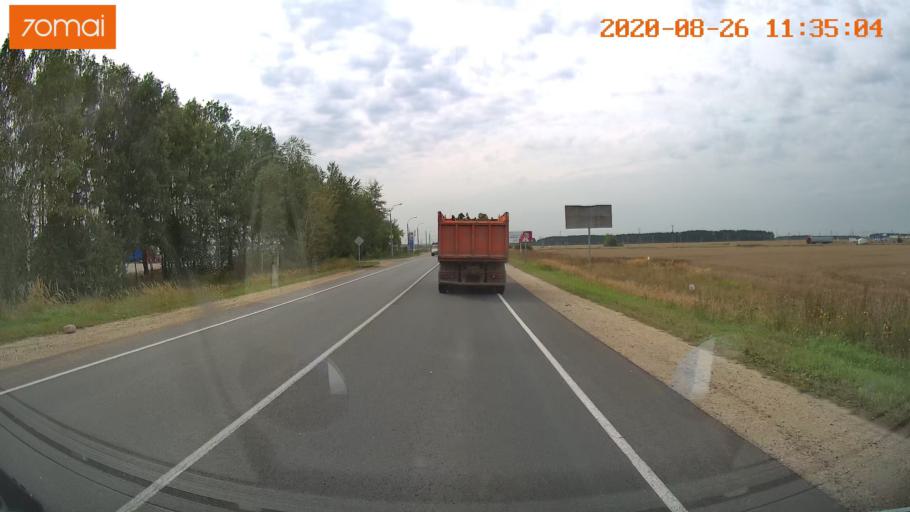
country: RU
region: Rjazan
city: Shilovo
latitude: 54.2785
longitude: 40.8376
